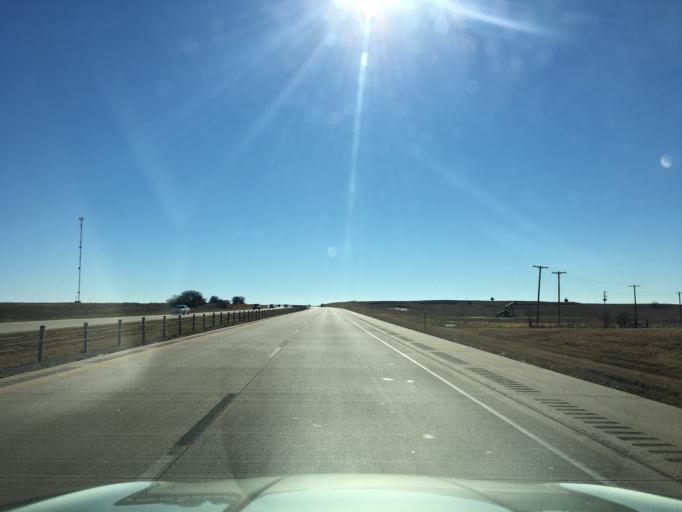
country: US
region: Oklahoma
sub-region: Kay County
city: Tonkawa
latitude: 36.5152
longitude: -97.3374
